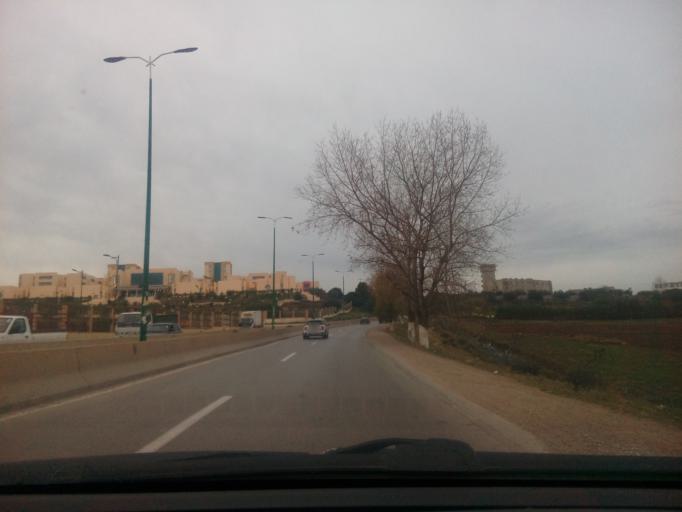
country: DZ
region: Tlemcen
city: Mansoura
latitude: 34.9010
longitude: -1.3490
